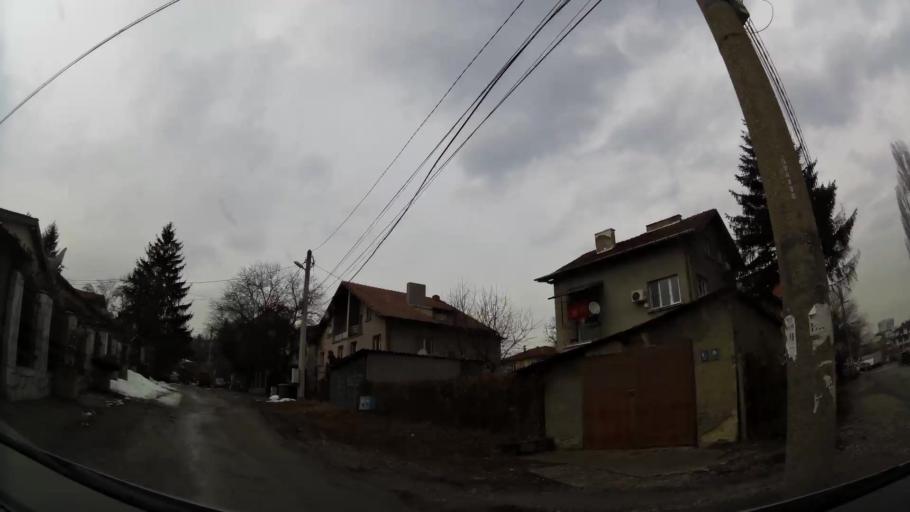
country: BG
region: Sofia-Capital
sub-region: Stolichna Obshtina
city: Sofia
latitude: 42.6662
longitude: 23.2475
